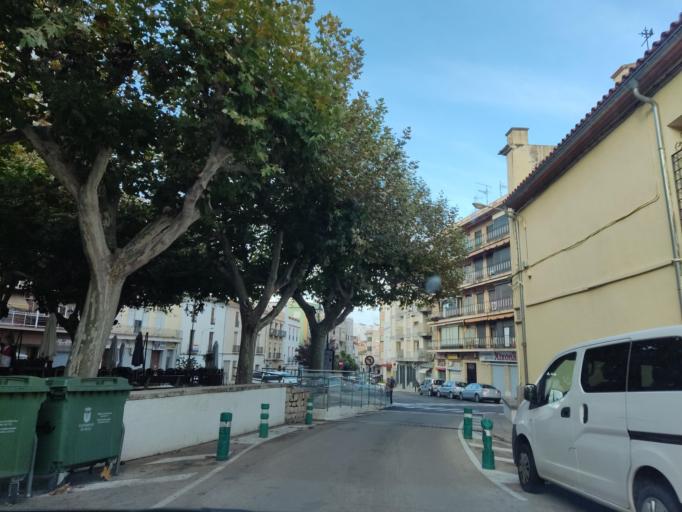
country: ES
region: Valencia
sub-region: Provincia de Alicante
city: Pego
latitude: 38.8398
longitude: -0.1197
